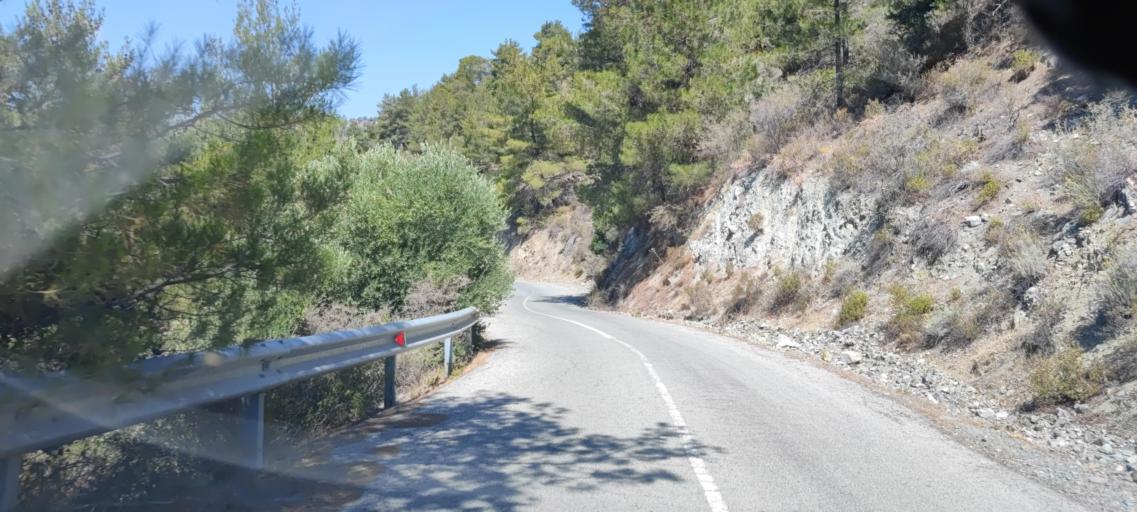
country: CY
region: Lefkosia
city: Kakopetria
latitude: 34.9234
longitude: 32.7978
